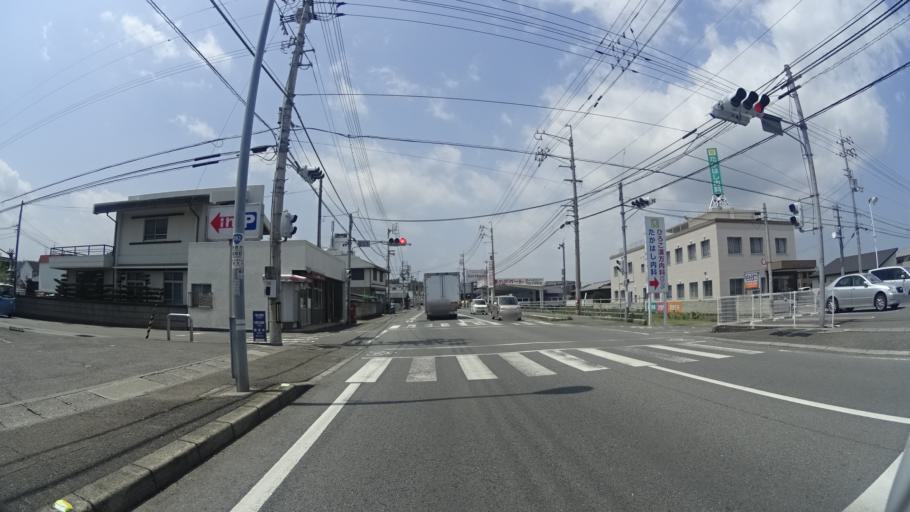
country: JP
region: Tokushima
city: Ishii
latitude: 34.0709
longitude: 134.4736
